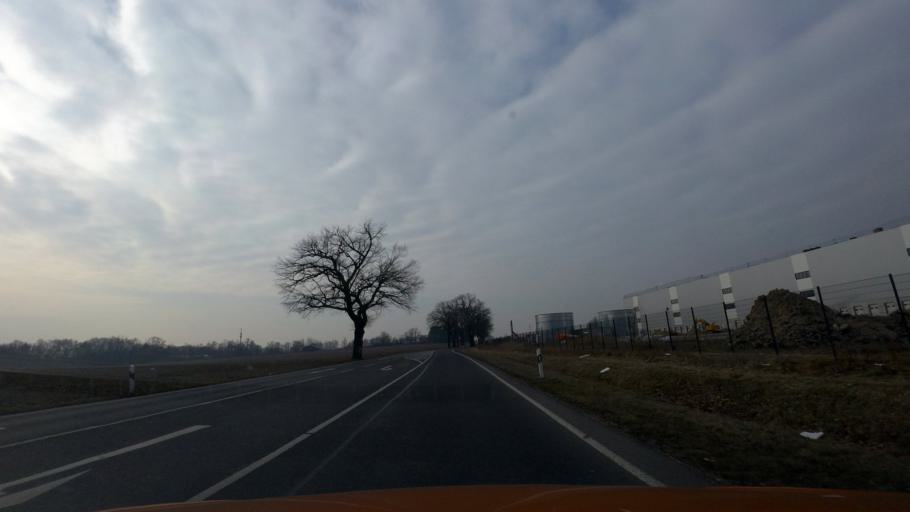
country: DE
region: Brandenburg
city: Trebbin
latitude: 52.2261
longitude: 13.2242
